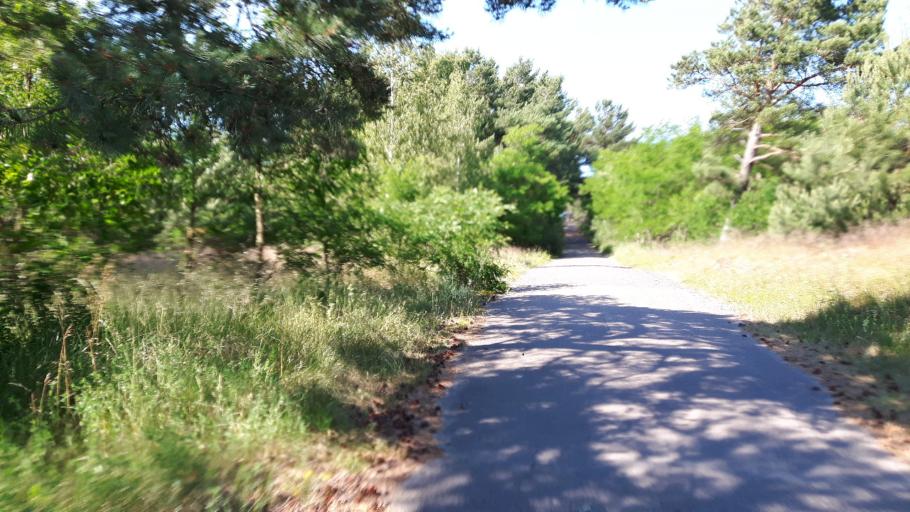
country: LT
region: Klaipedos apskritis
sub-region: Klaipeda
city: Klaipeda
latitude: 55.6924
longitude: 21.1030
